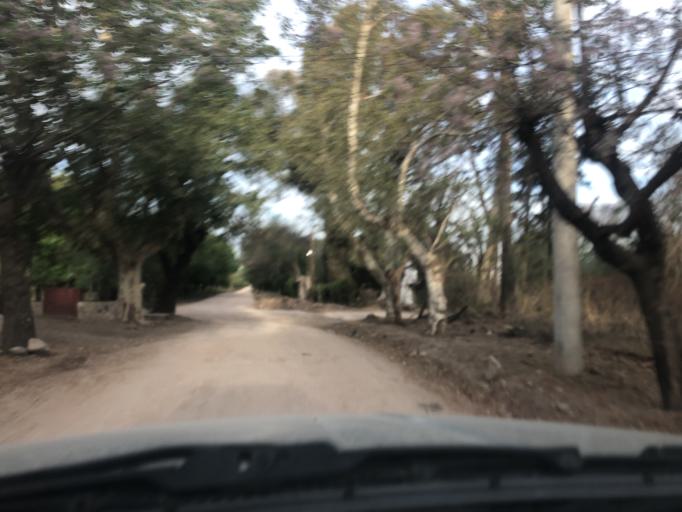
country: AR
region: Cordoba
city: La Granja
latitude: -31.0178
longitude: -64.2385
